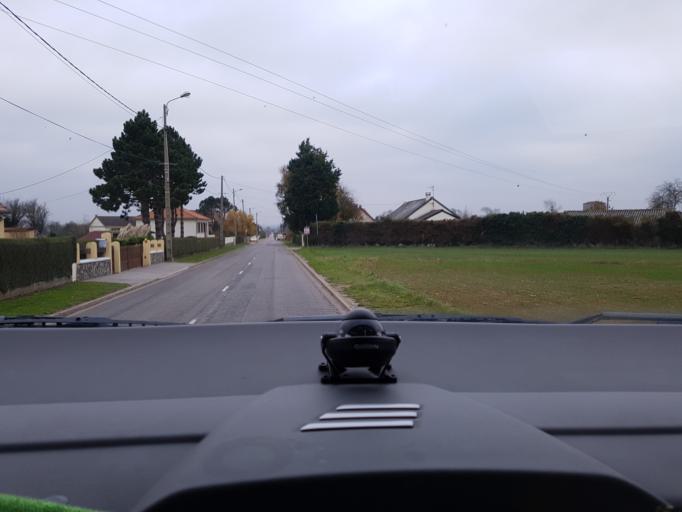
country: FR
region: Haute-Normandie
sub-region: Departement de la Seine-Maritime
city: Le Treport
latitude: 50.0436
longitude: 1.3653
